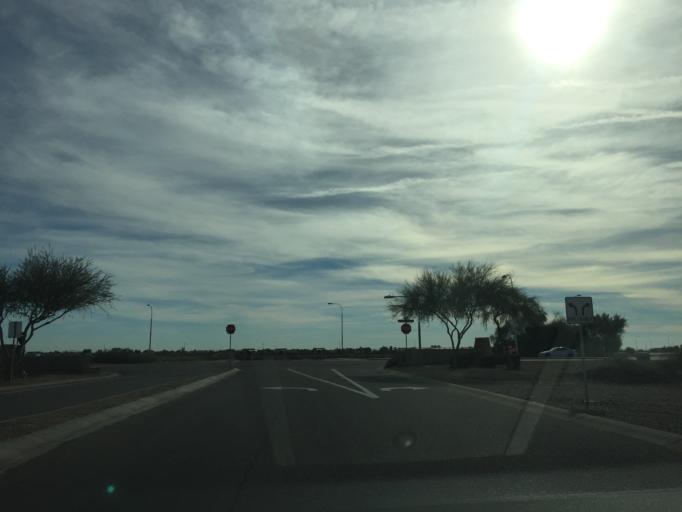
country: US
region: Arizona
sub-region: Maricopa County
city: Chandler
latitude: 33.2630
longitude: -111.8218
